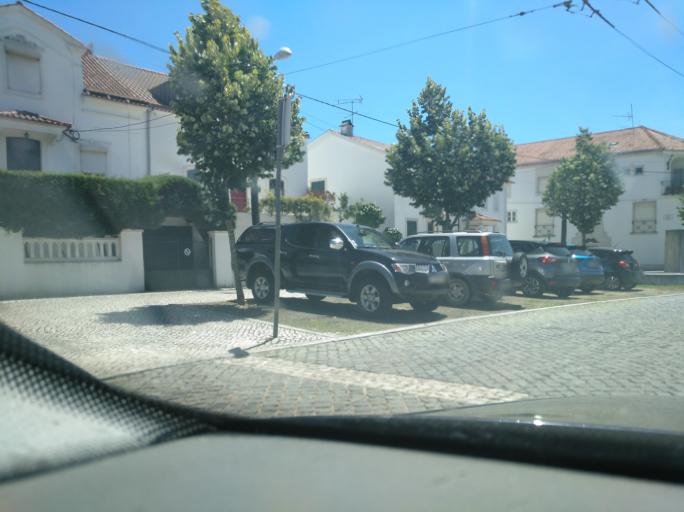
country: PT
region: Coimbra
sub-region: Coimbra
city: Coimbra
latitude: 40.2093
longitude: -8.4121
